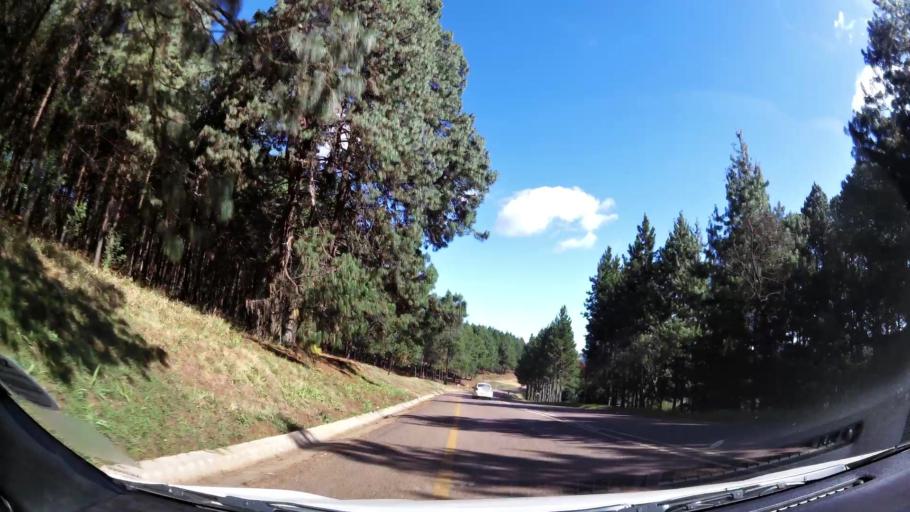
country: ZA
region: Limpopo
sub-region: Capricorn District Municipality
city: Mankoeng
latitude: -23.9050
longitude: 29.9874
